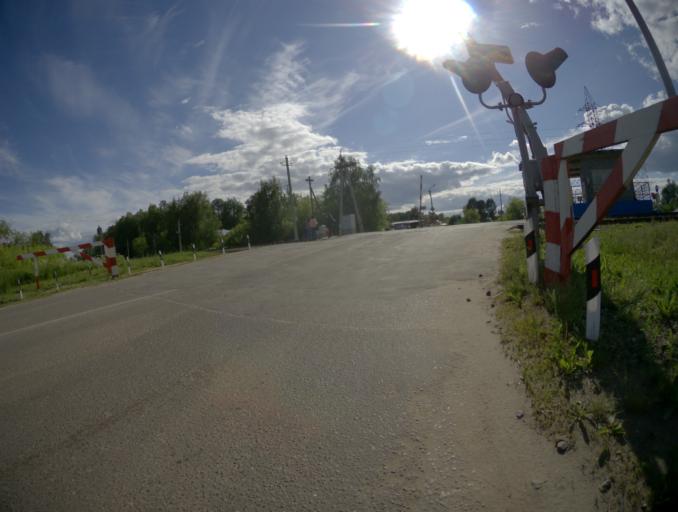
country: RU
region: Ivanovo
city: Shuya
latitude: 56.8412
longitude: 41.3504
